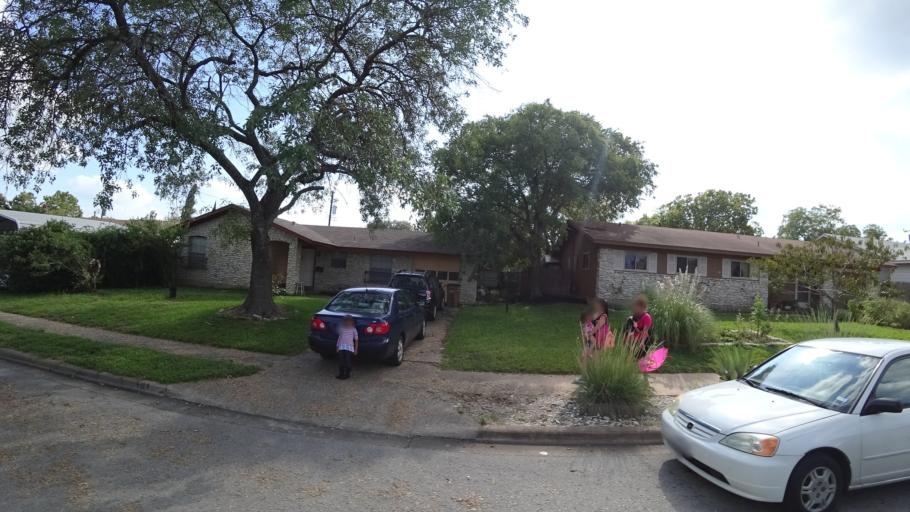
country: US
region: Texas
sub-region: Travis County
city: Wells Branch
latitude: 30.3588
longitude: -97.7036
